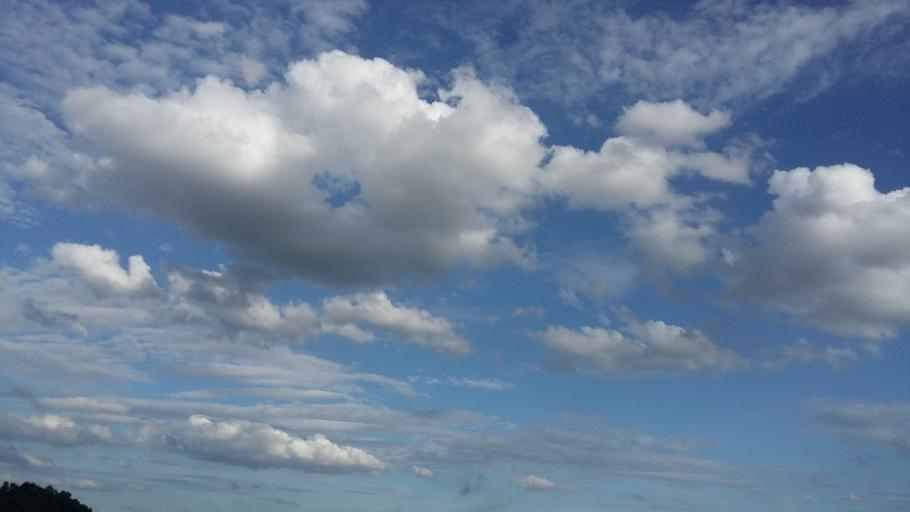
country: DE
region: Bavaria
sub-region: Swabia
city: Merching
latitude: 48.2412
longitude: 10.9982
